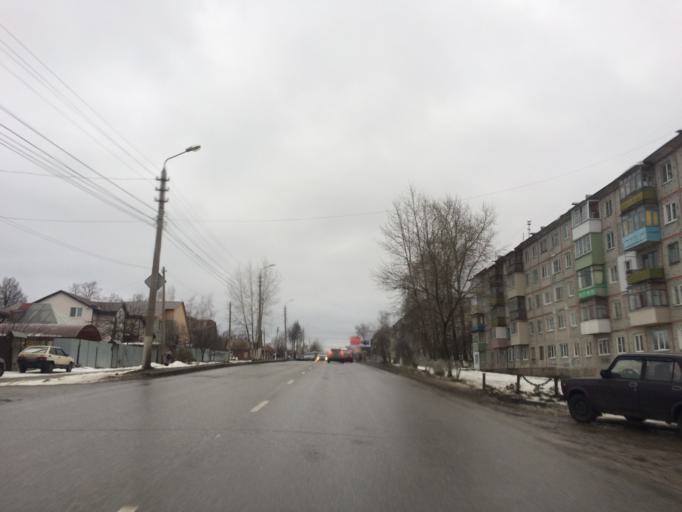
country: RU
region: Tula
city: Tula
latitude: 54.1993
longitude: 37.6853
